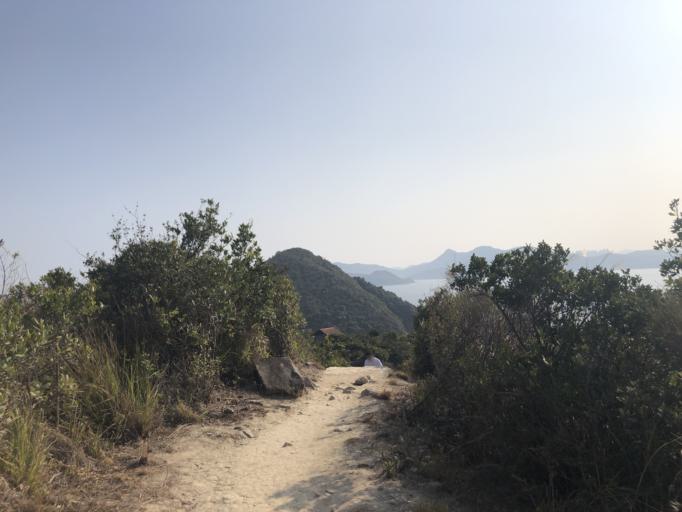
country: HK
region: Sai Kung
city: Sai Kung
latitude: 22.3587
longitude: 114.2955
